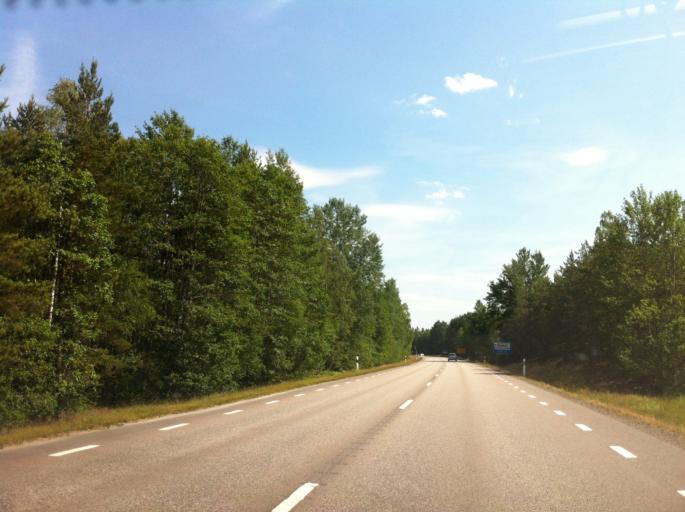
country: SE
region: Kalmar
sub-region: Nybro Kommun
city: Nybro
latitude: 56.8480
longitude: 15.6979
